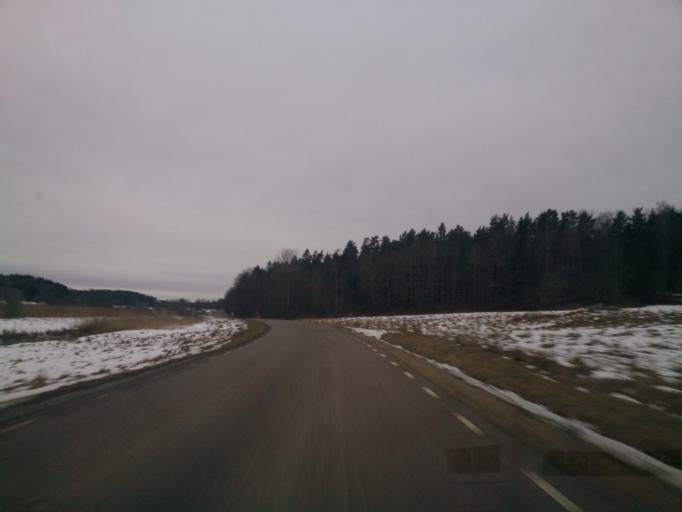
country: SE
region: OEstergoetland
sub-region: Atvidabergs Kommun
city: Atvidaberg
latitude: 58.2885
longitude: 16.0203
